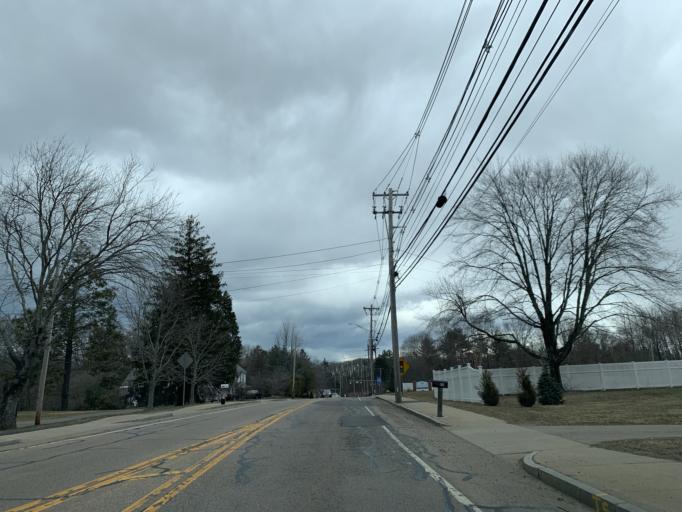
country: US
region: Massachusetts
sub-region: Norfolk County
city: Franklin
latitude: 42.0620
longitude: -71.4063
